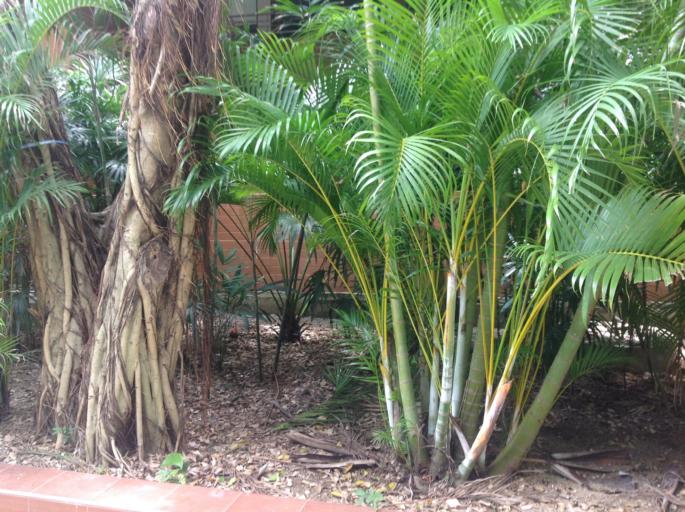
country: TH
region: Chiang Mai
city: Hang Dong
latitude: 18.7145
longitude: 98.9350
